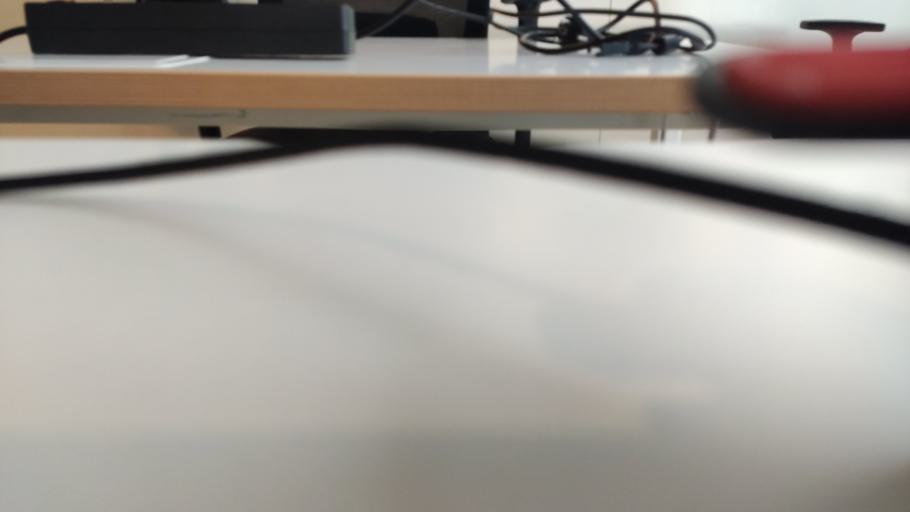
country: RU
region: Moskovskaya
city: Shevlyakovo
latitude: 56.4142
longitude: 36.9365
